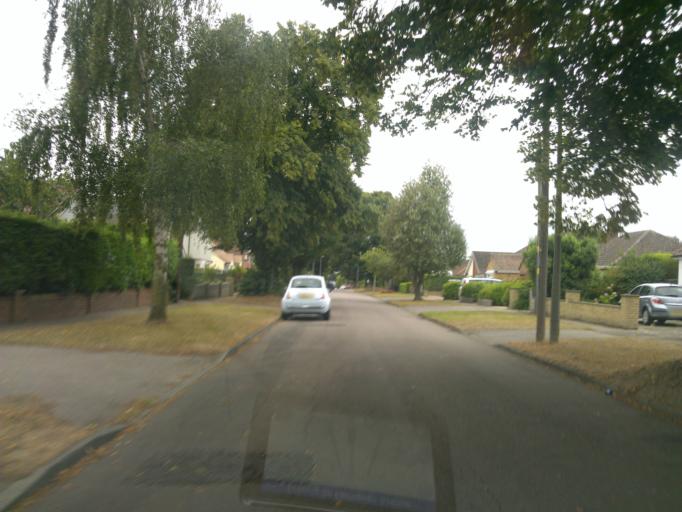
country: GB
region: England
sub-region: Essex
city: West Mersea
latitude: 51.7787
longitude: 0.9293
